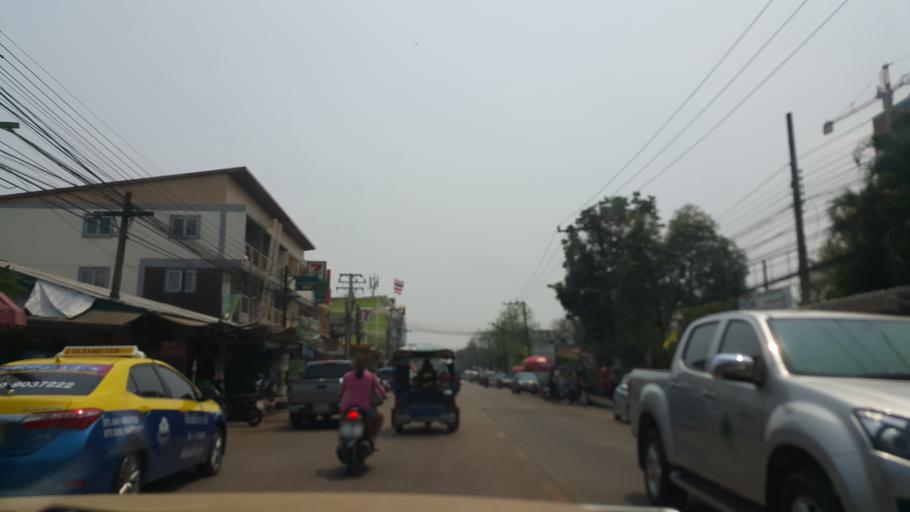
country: TH
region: Nakhon Phanom
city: Nakhon Phanom
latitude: 17.4142
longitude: 104.7780
